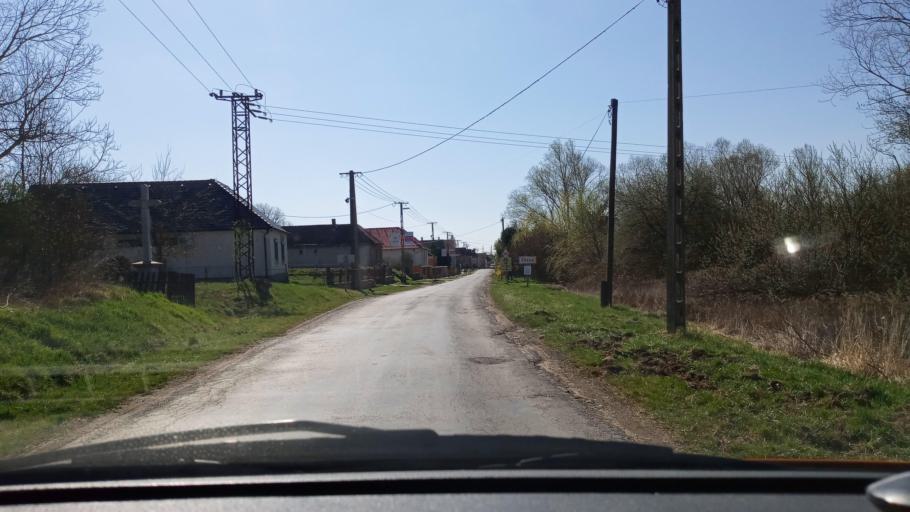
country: HU
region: Baranya
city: Kozarmisleny
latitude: 46.0633
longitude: 18.3731
